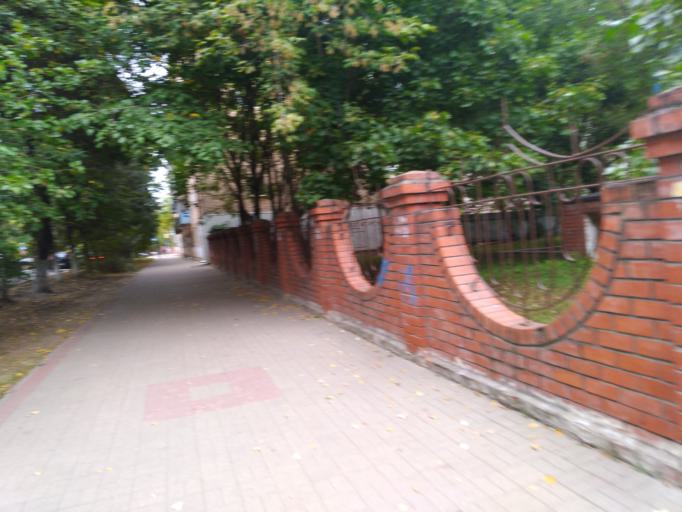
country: RU
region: Kaluga
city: Kaluga
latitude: 54.5331
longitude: 36.2590
